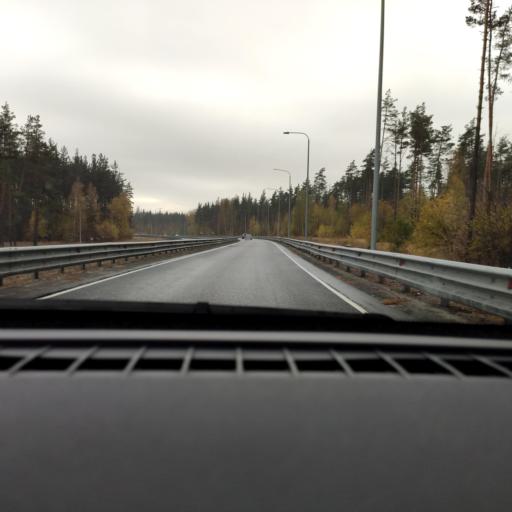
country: RU
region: Voronezj
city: Somovo
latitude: 51.6942
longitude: 39.3029
